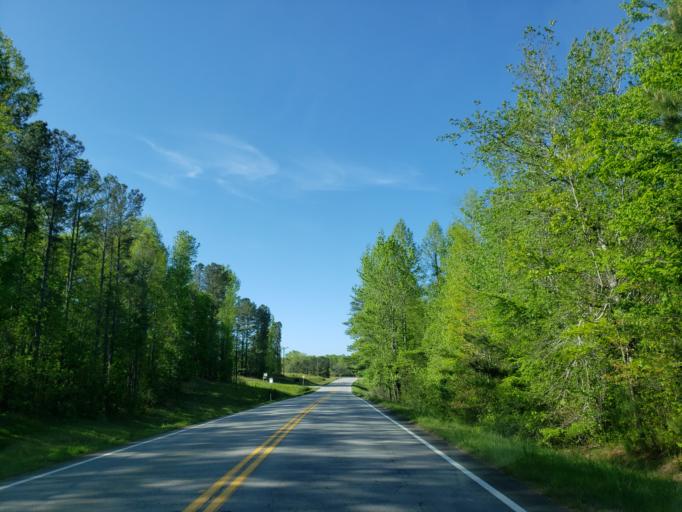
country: US
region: Georgia
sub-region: Haralson County
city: Tallapoosa
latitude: 33.8845
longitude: -85.3114
